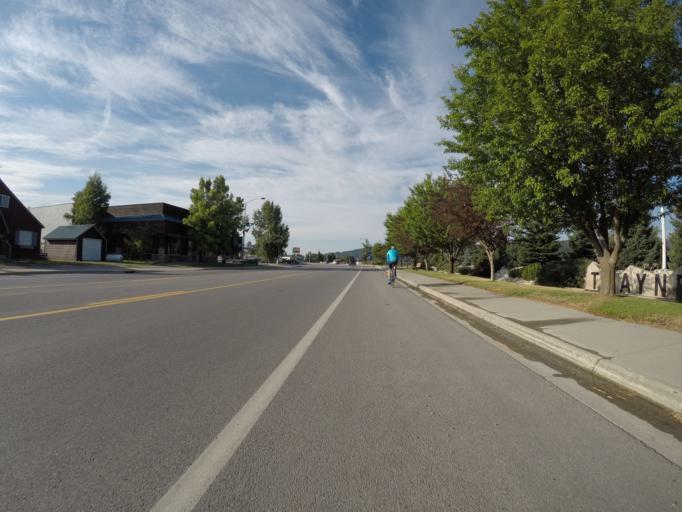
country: US
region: Wyoming
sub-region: Lincoln County
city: Afton
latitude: 42.9186
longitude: -111.0026
